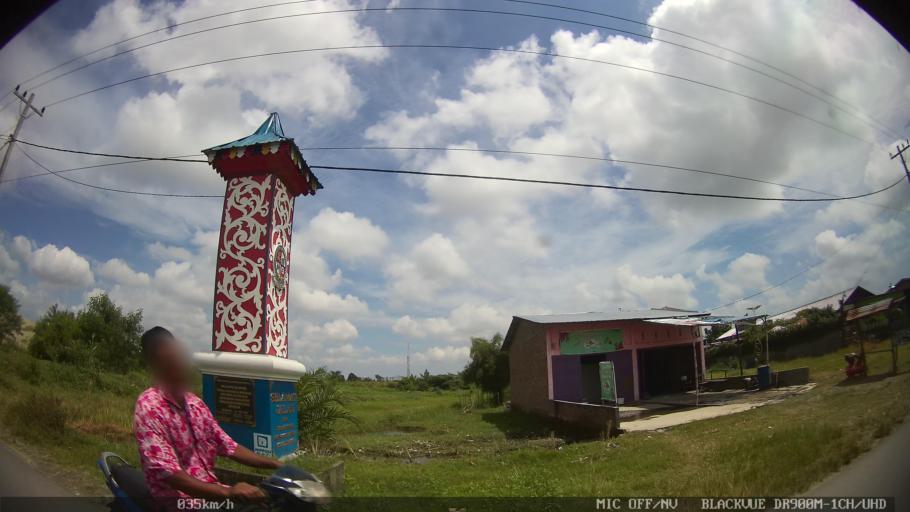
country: ID
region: North Sumatra
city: Percut
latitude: 3.6197
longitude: 98.7734
